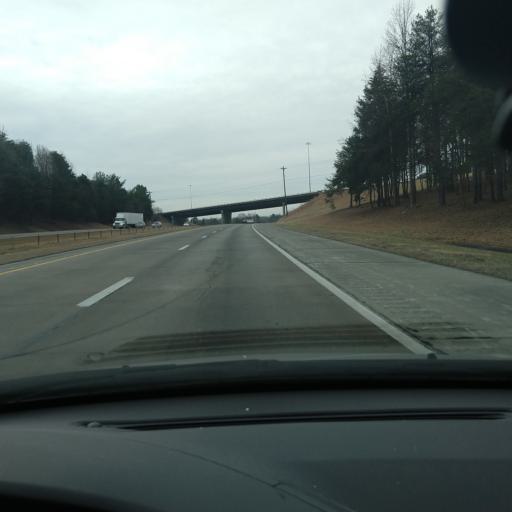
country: US
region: North Carolina
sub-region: Davidson County
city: Midway
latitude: 35.9724
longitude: -80.2304
